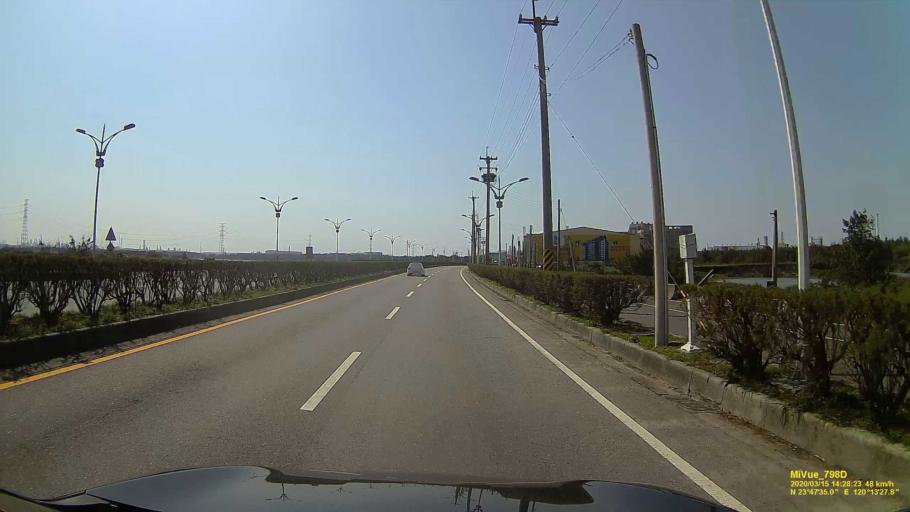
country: TW
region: Taiwan
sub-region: Yunlin
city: Douliu
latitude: 23.7931
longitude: 120.2238
